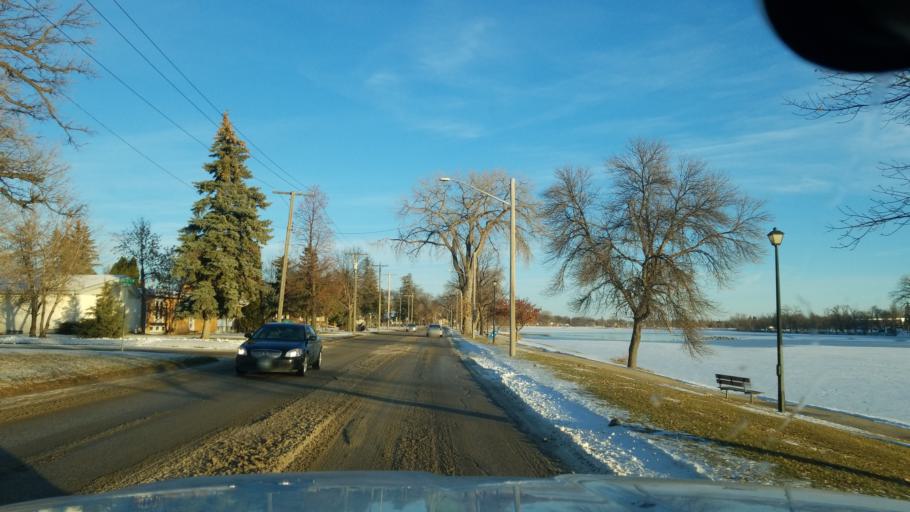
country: CA
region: Manitoba
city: Portage la Prairie
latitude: 49.9704
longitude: -98.3050
